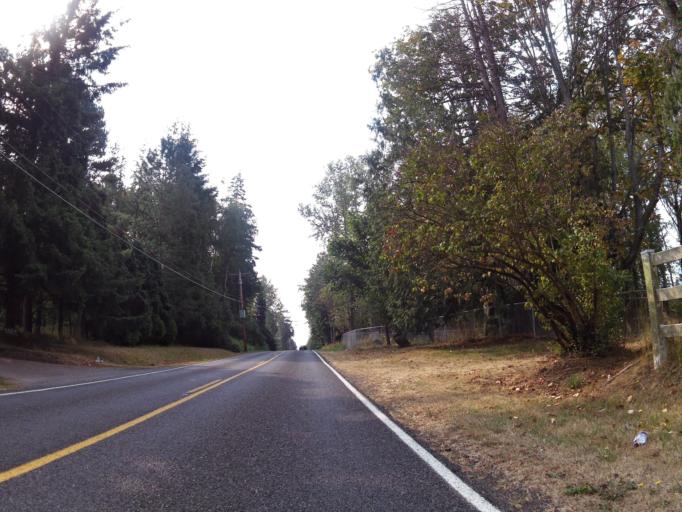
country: US
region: Washington
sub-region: Whatcom County
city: Ferndale
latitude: 48.8111
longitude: -122.6828
